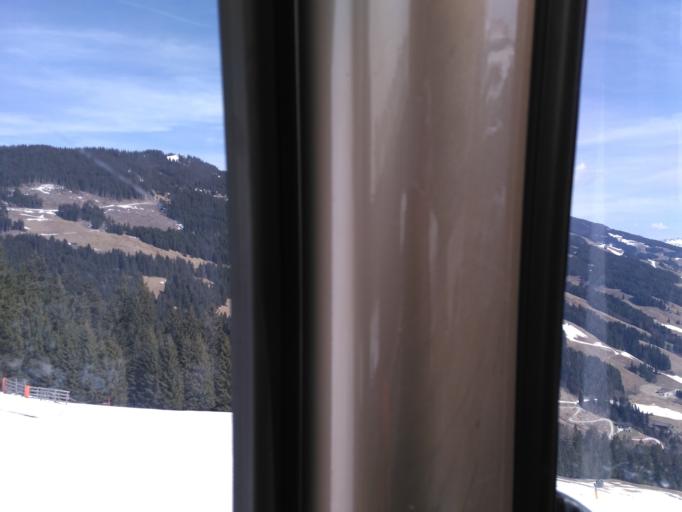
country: AT
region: Salzburg
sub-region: Politischer Bezirk Zell am See
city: Saalbach
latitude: 47.3999
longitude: 12.6233
